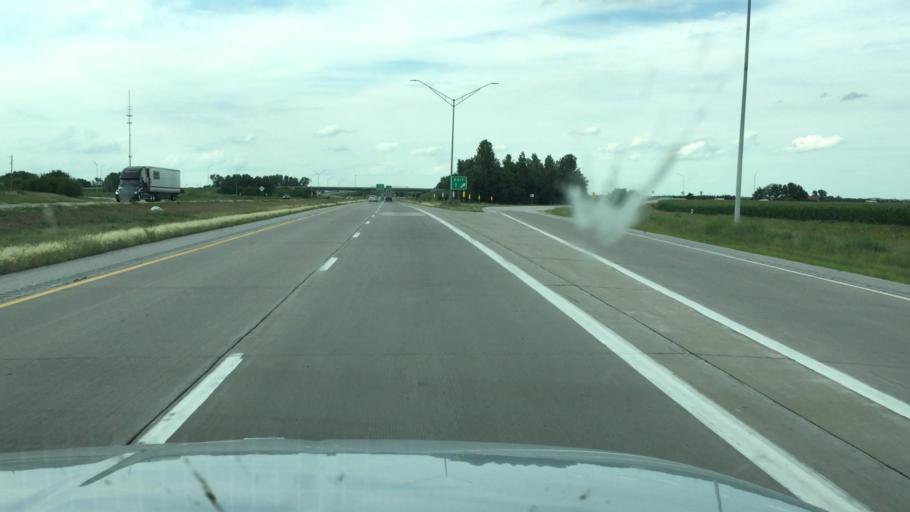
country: US
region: Iowa
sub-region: Scott County
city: Walcott
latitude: 41.5867
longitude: -90.6757
